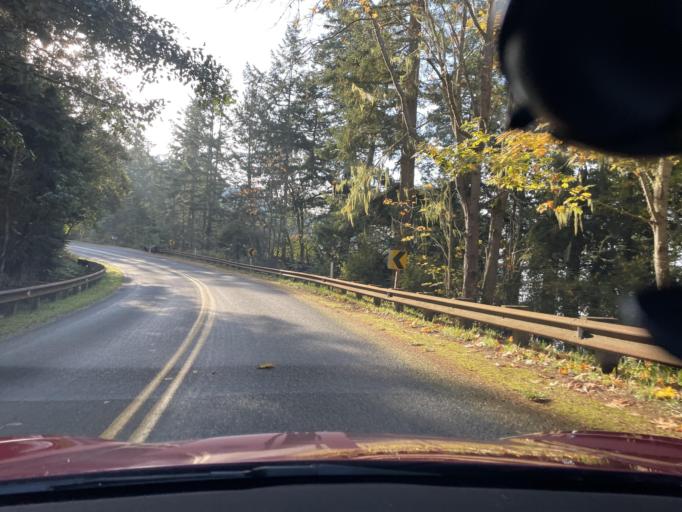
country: US
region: Washington
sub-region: San Juan County
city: Friday Harbor
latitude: 48.5512
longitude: -123.1645
